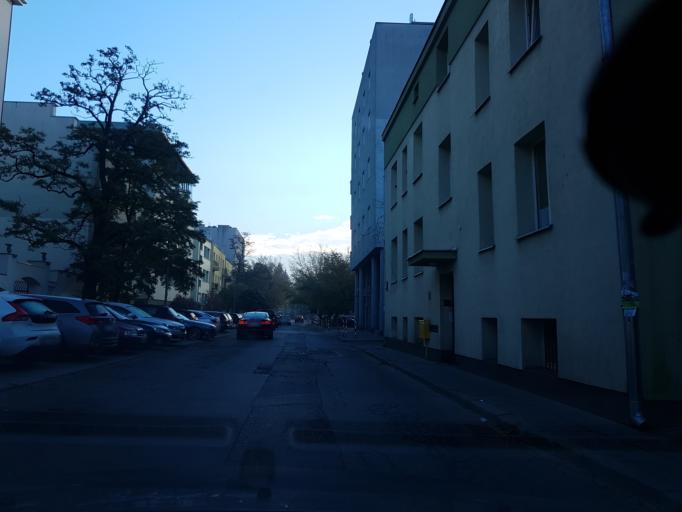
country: PL
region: Masovian Voivodeship
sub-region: Warszawa
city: Praga Poludnie
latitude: 52.2474
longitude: 21.0674
